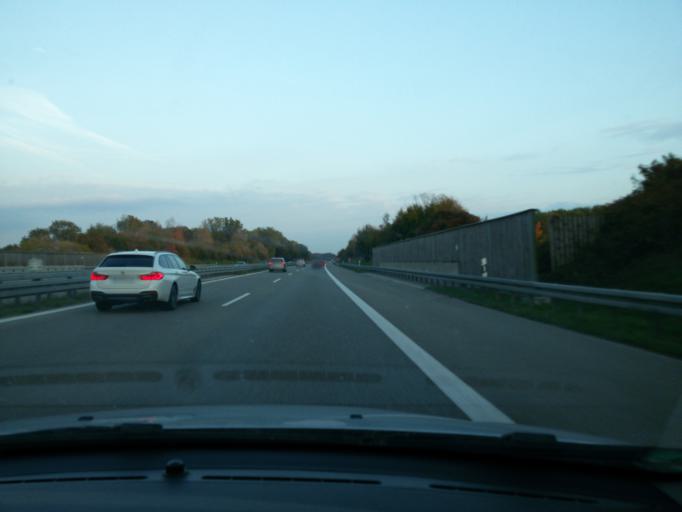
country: DE
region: Bavaria
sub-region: Swabia
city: Turkheim
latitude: 48.0387
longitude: 10.6403
